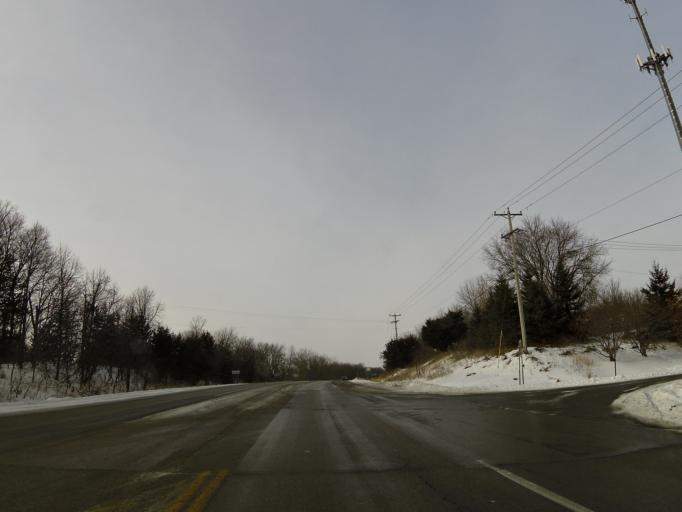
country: US
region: Minnesota
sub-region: Carver County
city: Victoria
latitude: 44.8914
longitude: -93.6661
